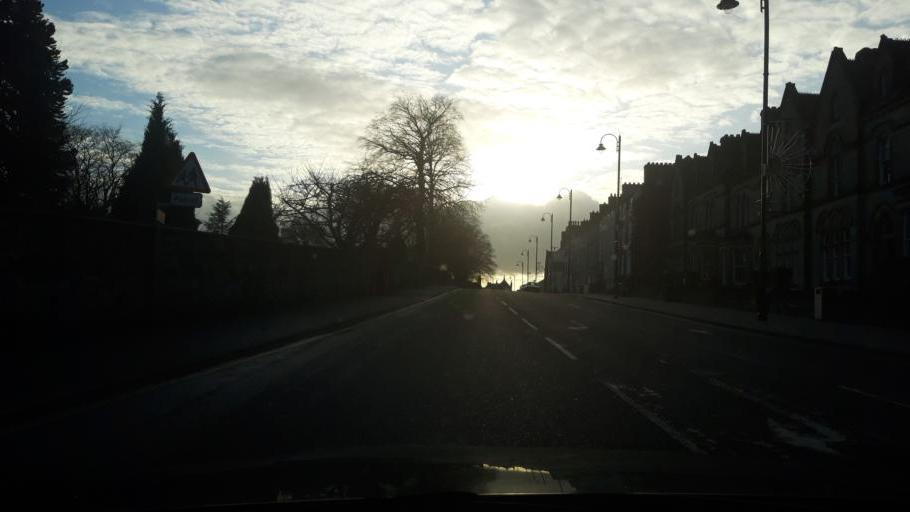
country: GB
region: Northern Ireland
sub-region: Dungannon District
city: Dungannon
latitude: 54.5050
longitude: -6.7643
